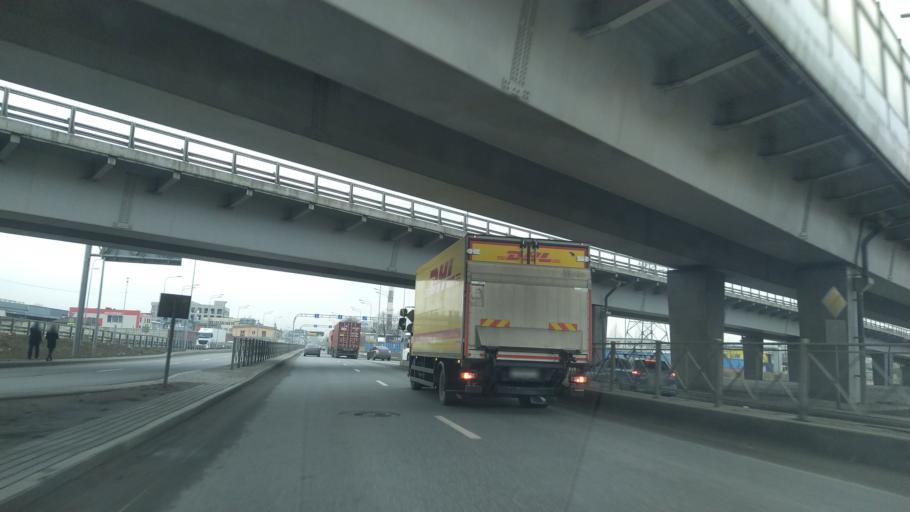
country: RU
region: St.-Petersburg
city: Kupchino
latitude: 59.8324
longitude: 30.3102
